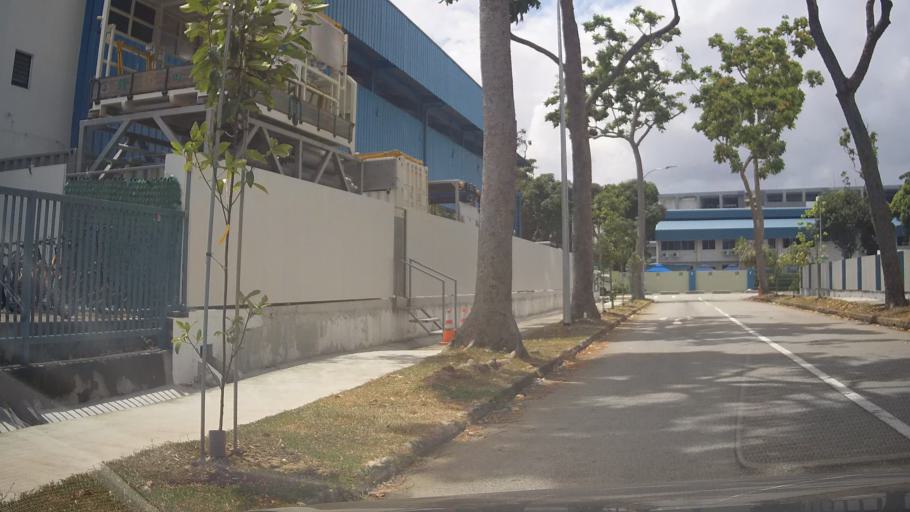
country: MY
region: Johor
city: Kampung Pasir Gudang Baru
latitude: 1.3832
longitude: 103.9725
